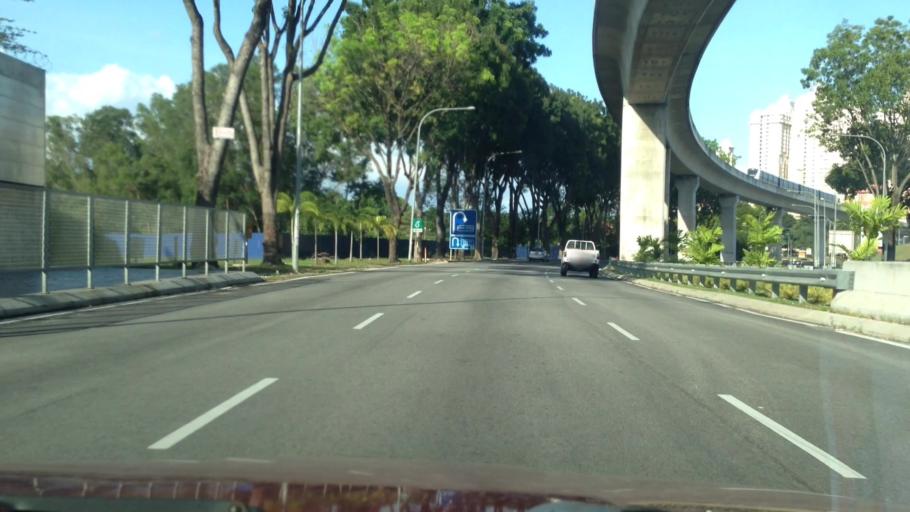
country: MY
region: Selangor
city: Subang Jaya
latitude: 3.0301
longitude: 101.5821
